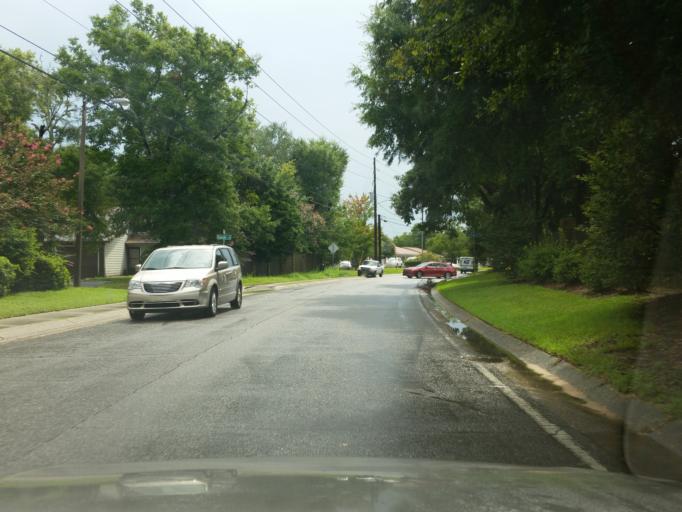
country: US
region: Florida
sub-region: Escambia County
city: Ferry Pass
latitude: 30.5015
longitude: -87.1878
